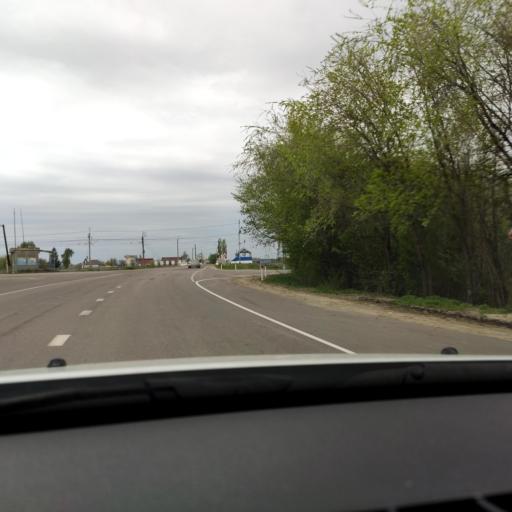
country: RU
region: Voronezj
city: Novovoronezh
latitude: 51.3625
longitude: 39.2921
